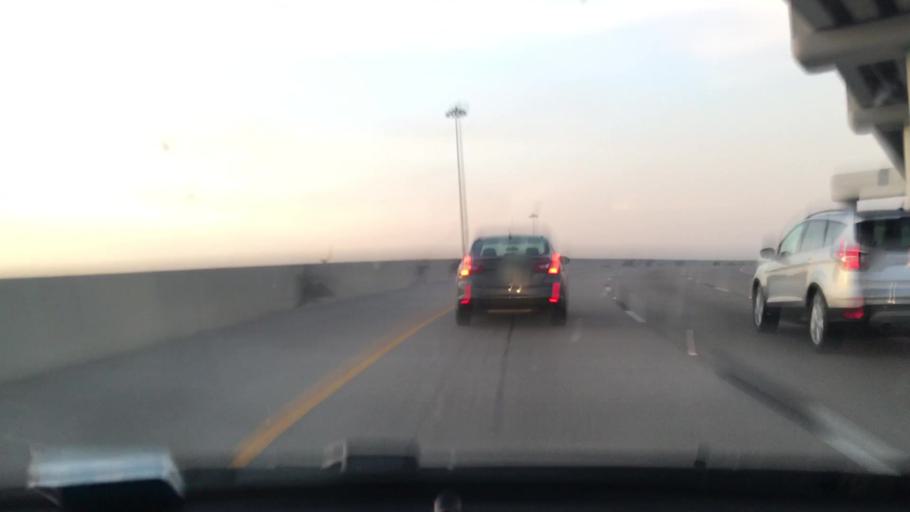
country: US
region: Texas
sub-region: Dallas County
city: Dallas
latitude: 32.7684
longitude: -96.8065
